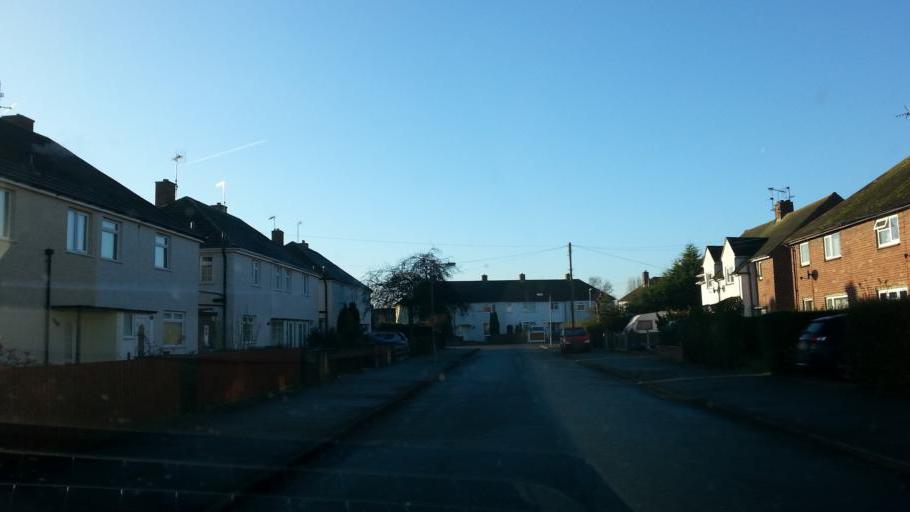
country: GB
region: England
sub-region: Nottinghamshire
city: Newark on Trent
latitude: 53.0640
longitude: -0.8174
